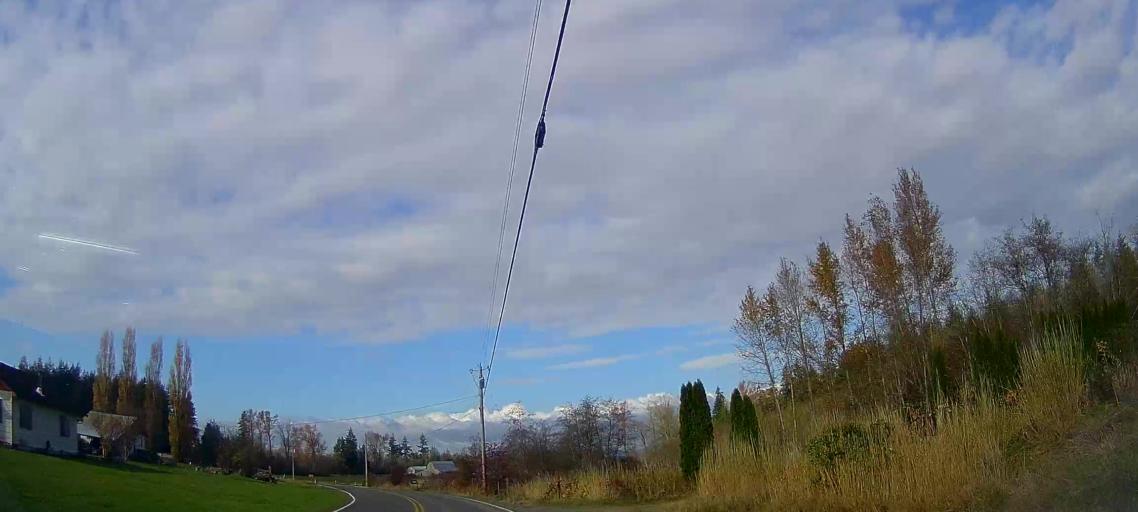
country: US
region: Washington
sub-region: Skagit County
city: Big Lake
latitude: 48.4272
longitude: -122.2404
